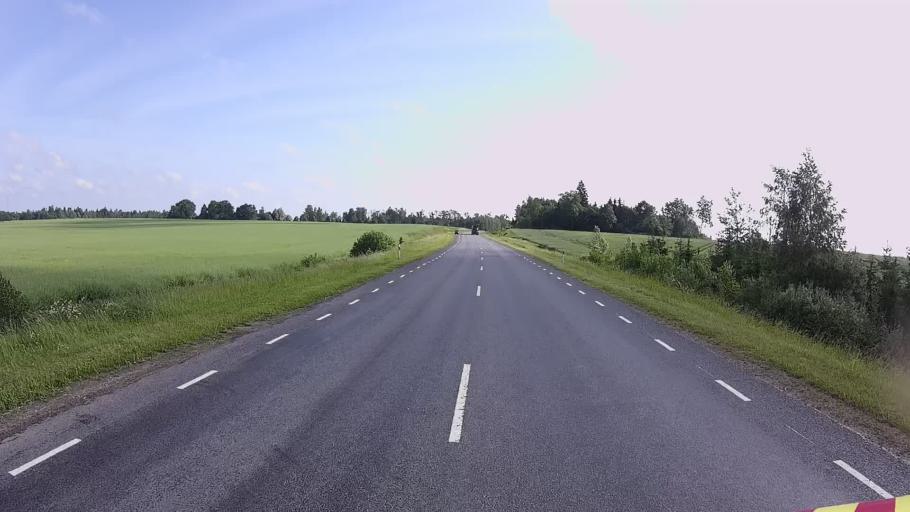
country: EE
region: Viljandimaa
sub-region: Viiratsi vald
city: Viiratsi
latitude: 58.3339
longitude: 25.6164
